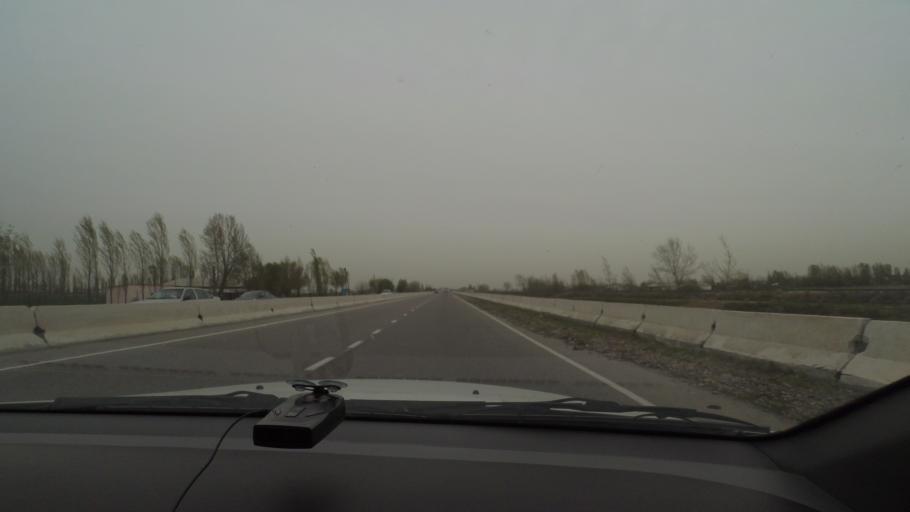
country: UZ
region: Jizzax
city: Gagarin
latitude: 40.4884
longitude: 68.2945
